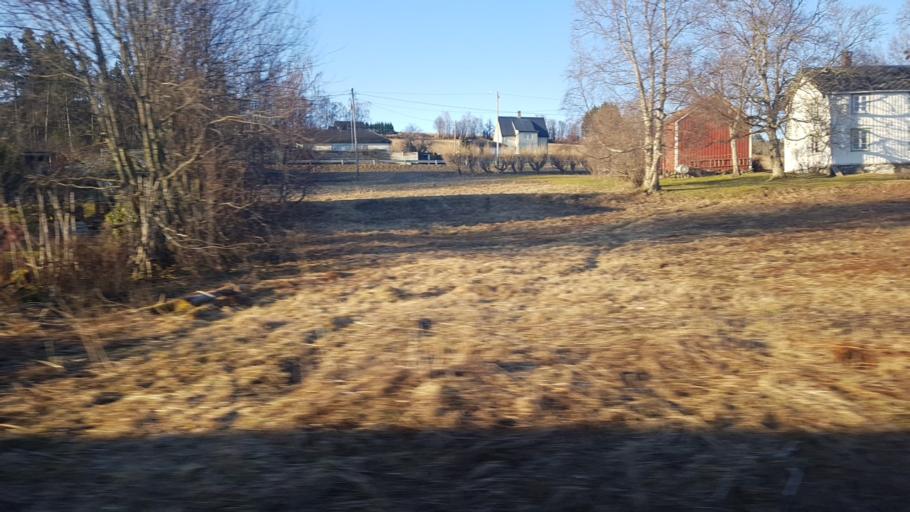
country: NO
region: Sor-Trondelag
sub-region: Malvik
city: Malvik
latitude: 63.4301
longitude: 10.6962
